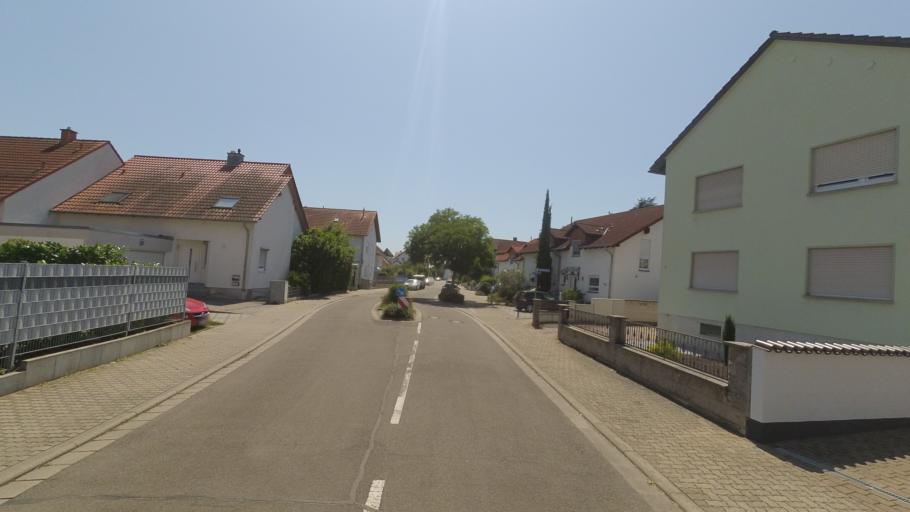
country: DE
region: Rheinland-Pfalz
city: Schifferstadt
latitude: 49.3965
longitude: 8.3745
